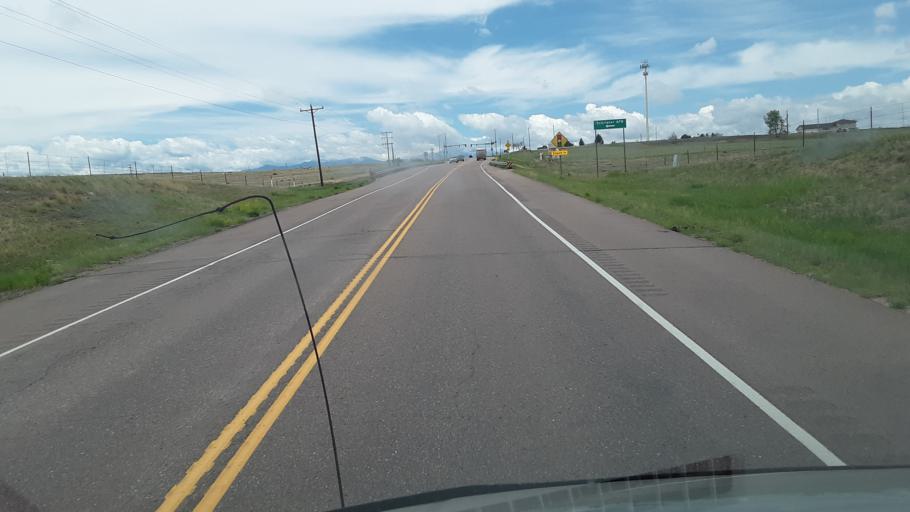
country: US
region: Colorado
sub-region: El Paso County
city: Ellicott
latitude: 38.8386
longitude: -104.5305
